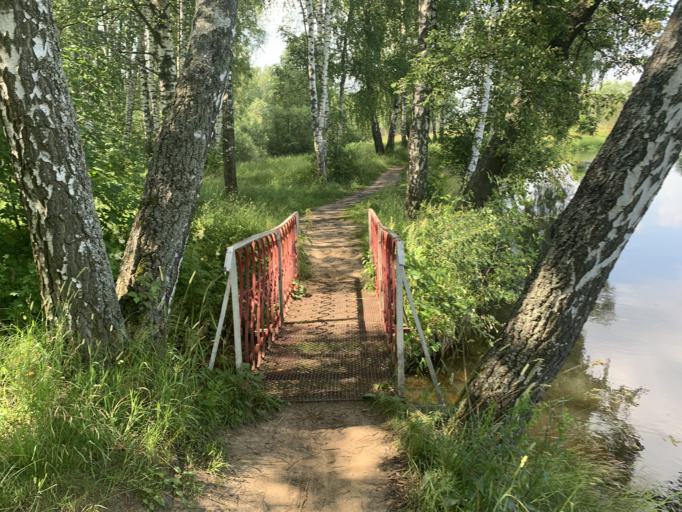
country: RU
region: Moskovskaya
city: Cherkizovo
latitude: 55.9738
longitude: 37.8010
